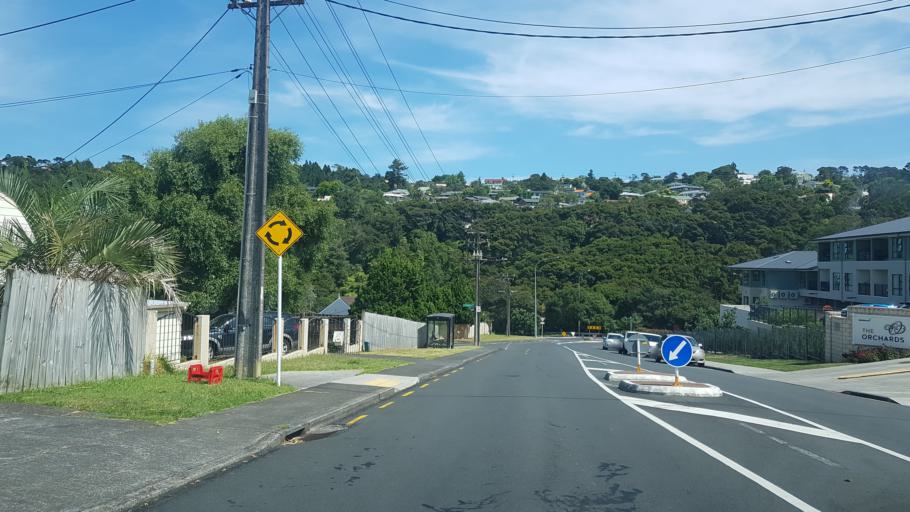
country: NZ
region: Auckland
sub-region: Auckland
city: North Shore
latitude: -36.7831
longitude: 174.7118
